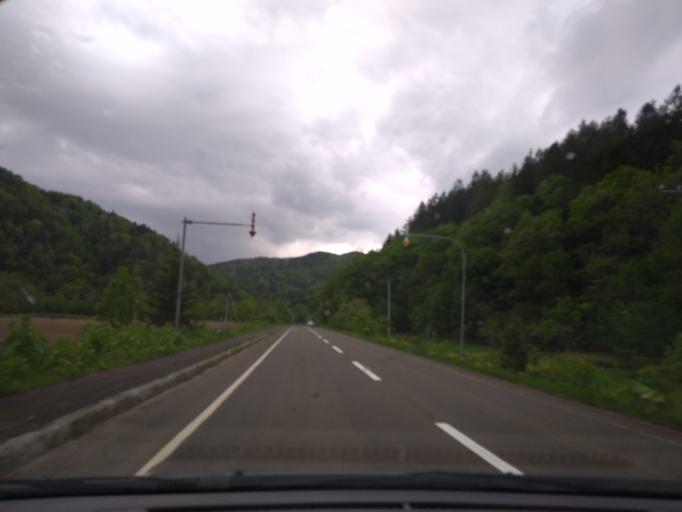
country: JP
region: Hokkaido
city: Shimo-furano
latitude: 43.1243
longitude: 142.4059
